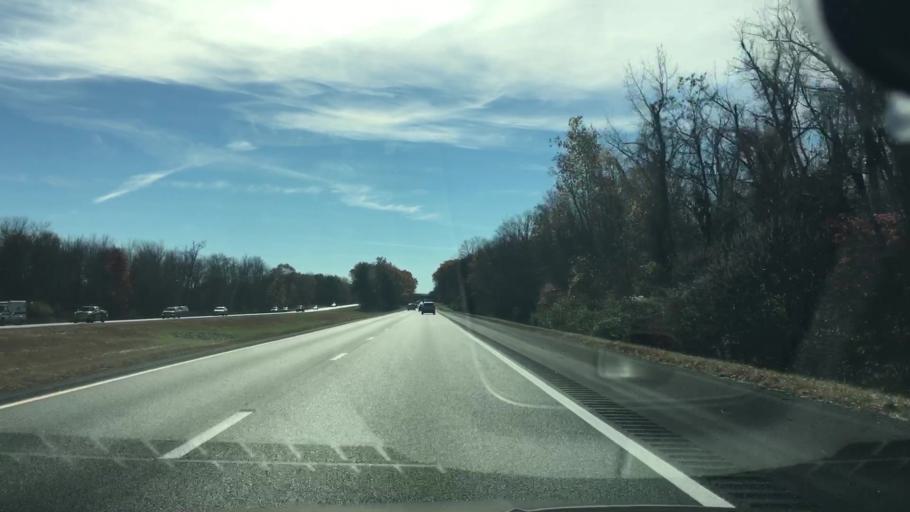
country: US
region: Massachusetts
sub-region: Franklin County
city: Whately
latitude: 42.4072
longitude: -72.6270
